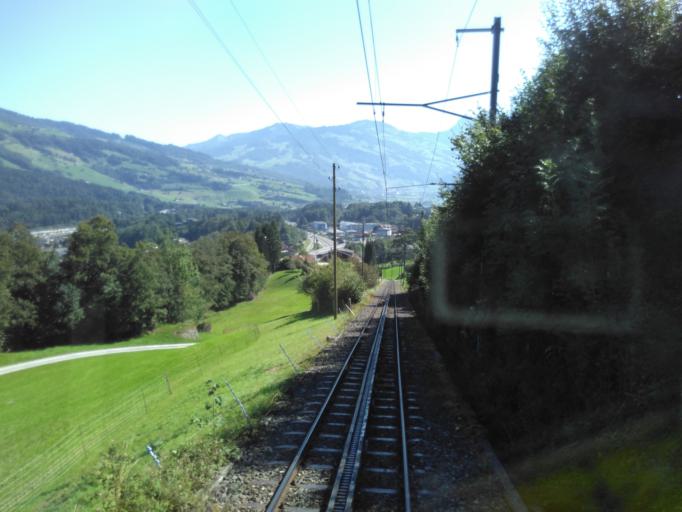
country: CH
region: Schwyz
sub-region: Bezirk Schwyz
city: Goldau
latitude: 47.0414
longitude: 8.5418
